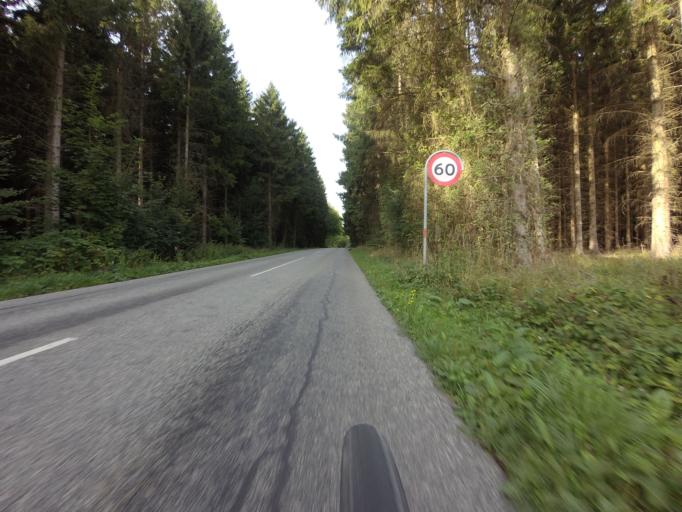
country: DK
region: Zealand
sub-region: Faxe Kommune
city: Fakse Ladeplads
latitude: 55.2274
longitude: 12.1979
